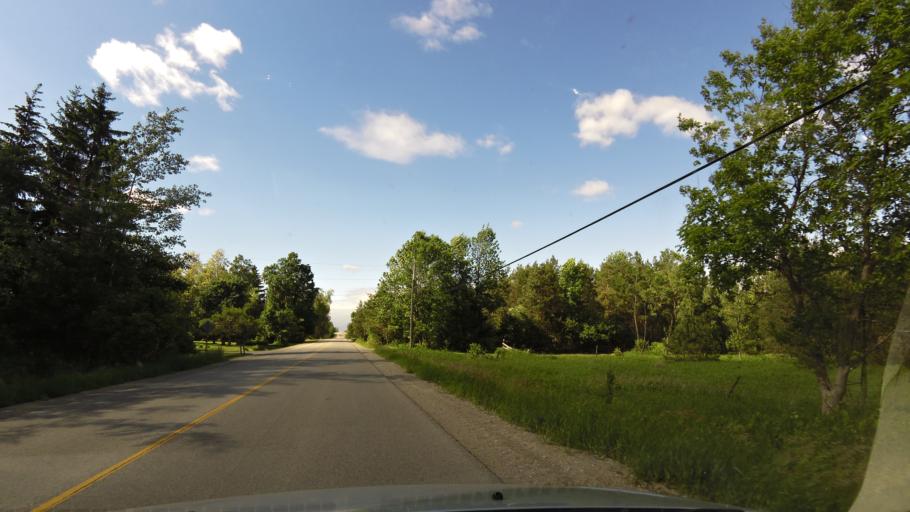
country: CA
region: Ontario
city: Bradford West Gwillimbury
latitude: 44.1868
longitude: -79.6216
